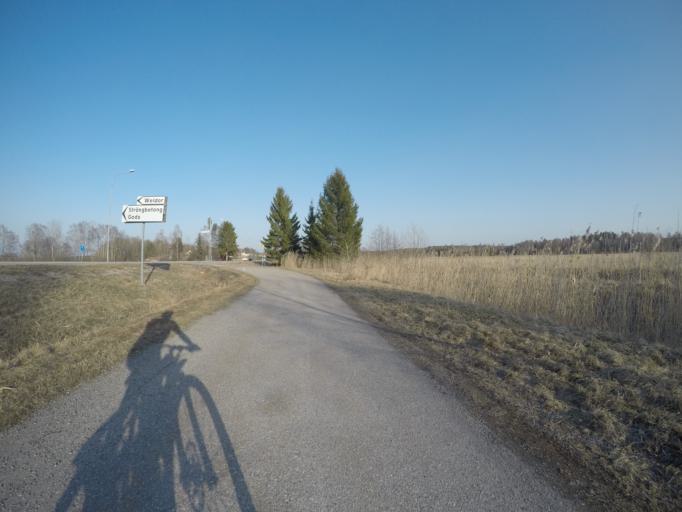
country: SE
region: Vaestmanland
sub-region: Kungsors Kommun
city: Kungsoer
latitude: 59.4232
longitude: 16.1351
